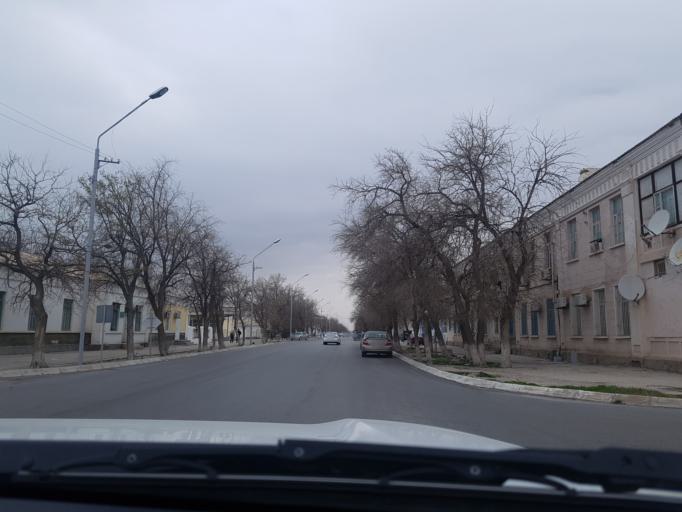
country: TM
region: Balkan
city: Balkanabat
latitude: 39.5025
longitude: 54.3661
